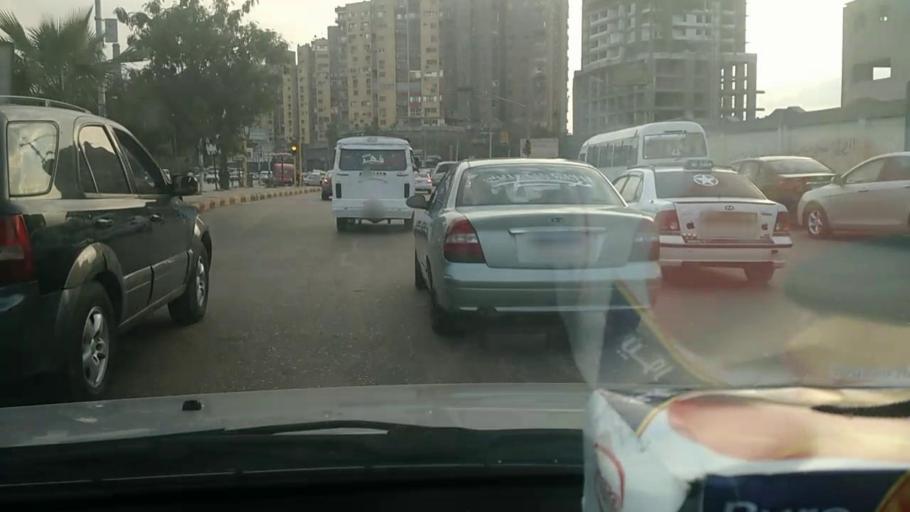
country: EG
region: Al Jizah
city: Al Jizah
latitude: 30.0008
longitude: 31.2145
